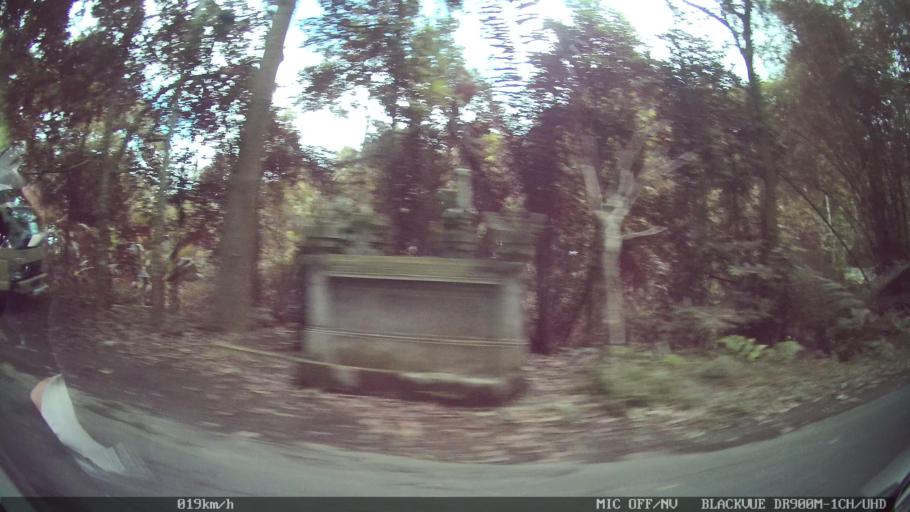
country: ID
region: Bali
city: Bangli
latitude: -8.4509
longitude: 115.3445
